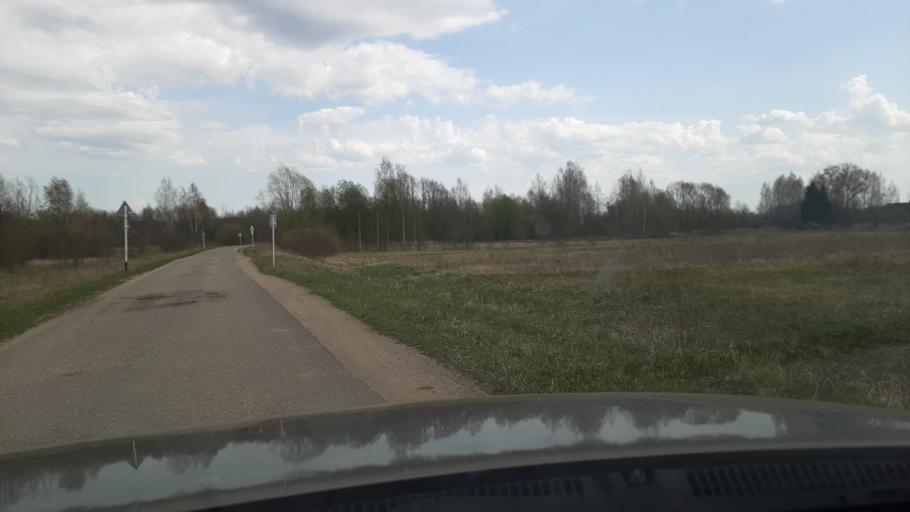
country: RU
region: Ivanovo
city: Furmanov
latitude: 57.3021
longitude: 41.1631
